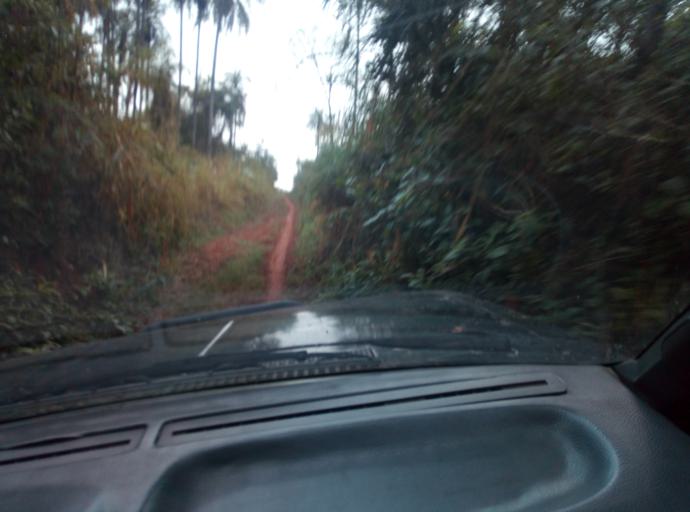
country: PY
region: Caaguazu
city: Carayao
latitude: -25.1936
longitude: -56.3544
